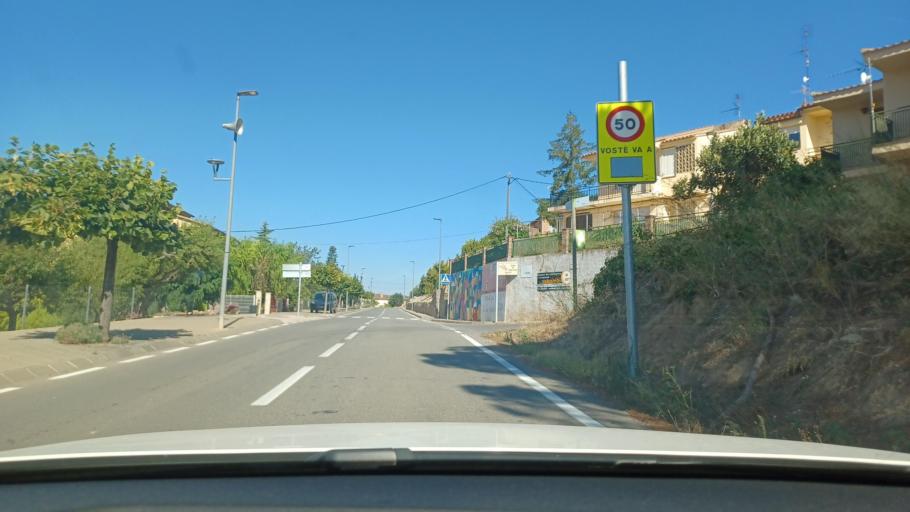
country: ES
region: Catalonia
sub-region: Provincia de Tarragona
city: Horta de Sant Joan
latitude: 40.9515
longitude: 0.3178
